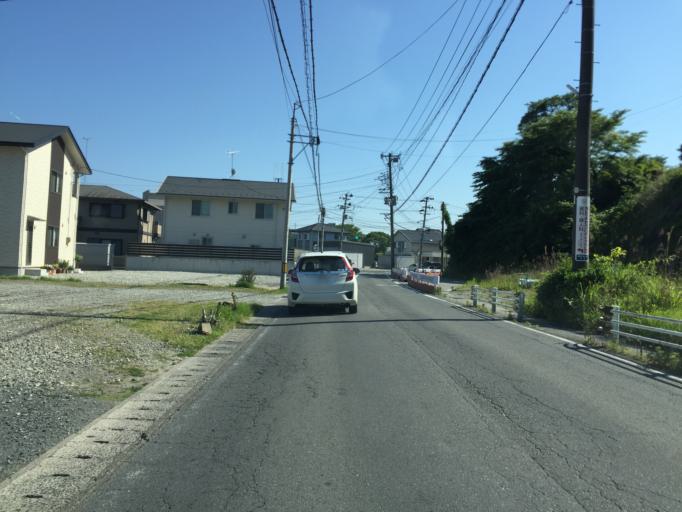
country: JP
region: Fukushima
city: Iwaki
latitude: 36.9891
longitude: 140.8539
